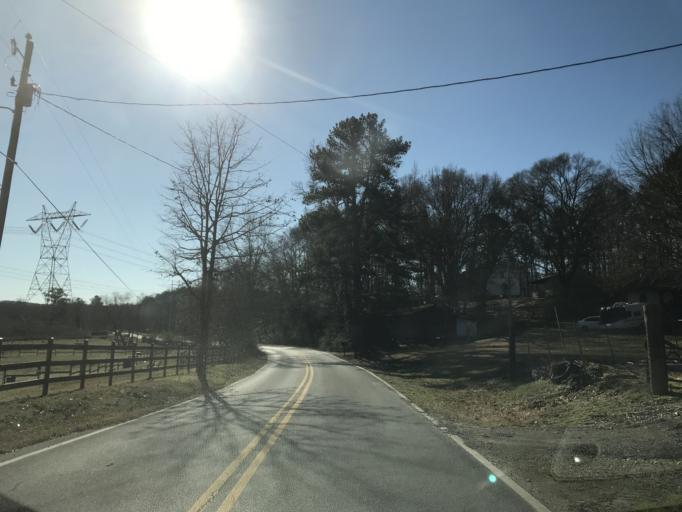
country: US
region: Georgia
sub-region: Paulding County
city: Dallas
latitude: 33.9995
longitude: -84.8969
